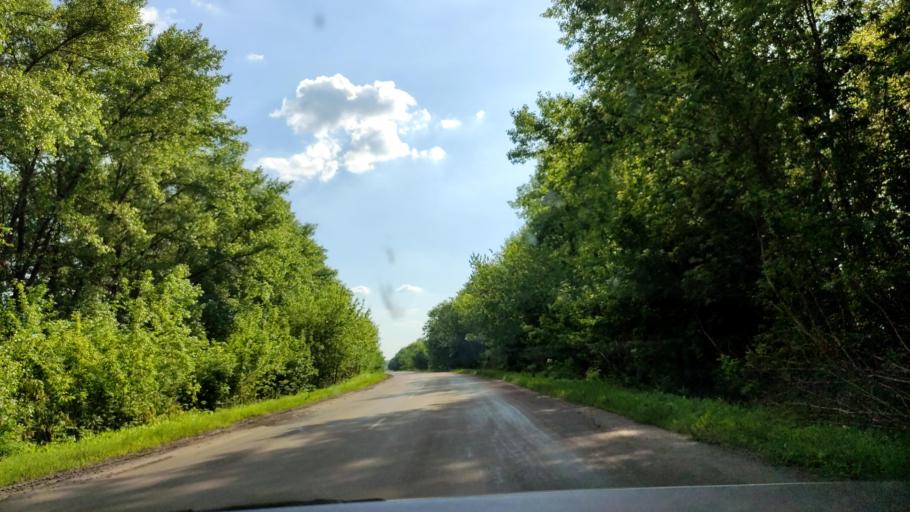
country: RU
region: Voronezj
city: Panino
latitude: 51.6183
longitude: 40.0179
